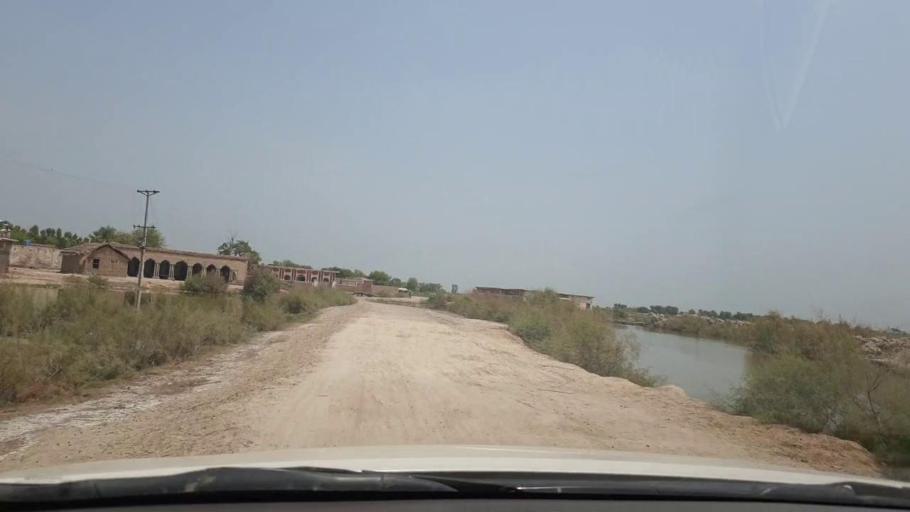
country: PK
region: Sindh
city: Rustam jo Goth
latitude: 28.0268
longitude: 68.7885
